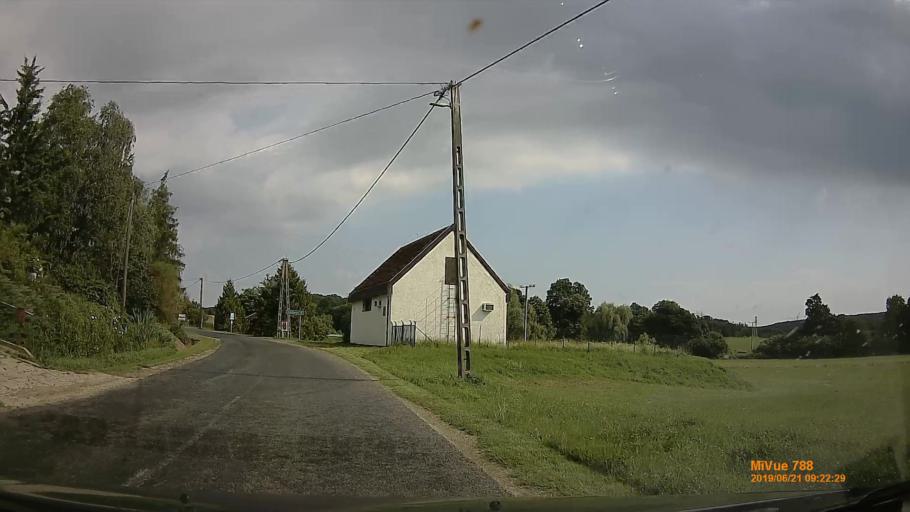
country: HU
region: Somogy
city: Taszar
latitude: 46.2466
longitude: 17.8910
